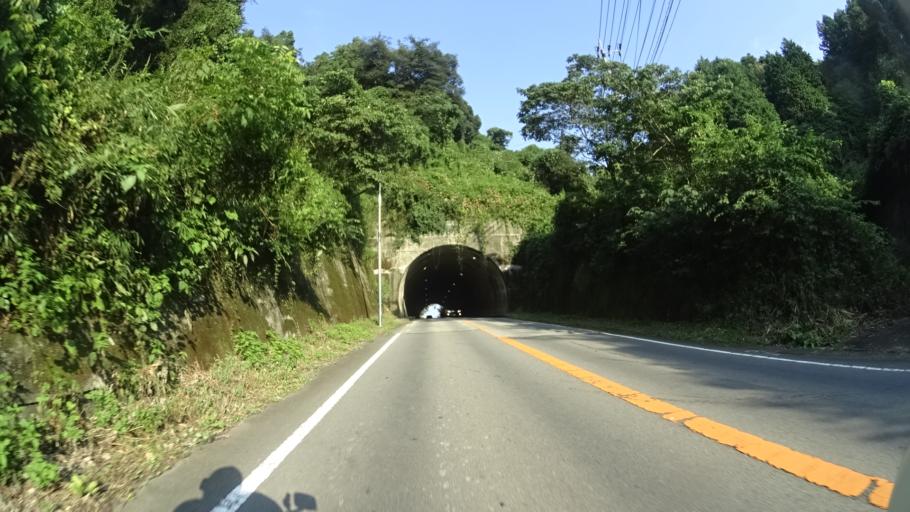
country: JP
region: Oita
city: Bungo-Takada-shi
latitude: 33.4458
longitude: 131.3393
